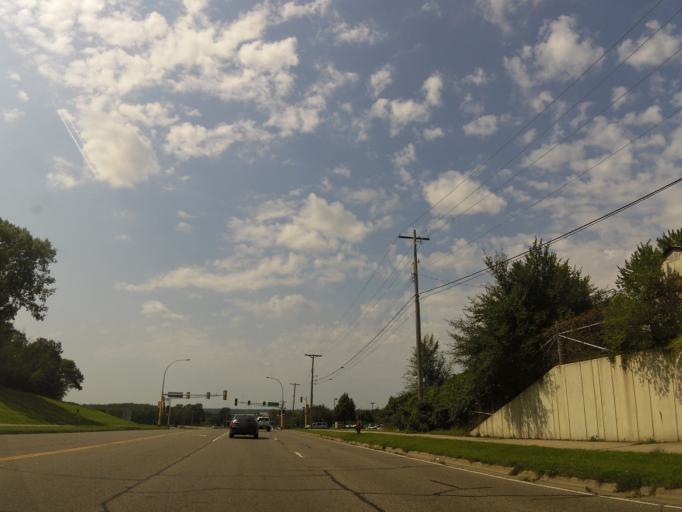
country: US
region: Minnesota
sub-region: Dakota County
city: Eagan
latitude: 44.8336
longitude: -93.1860
